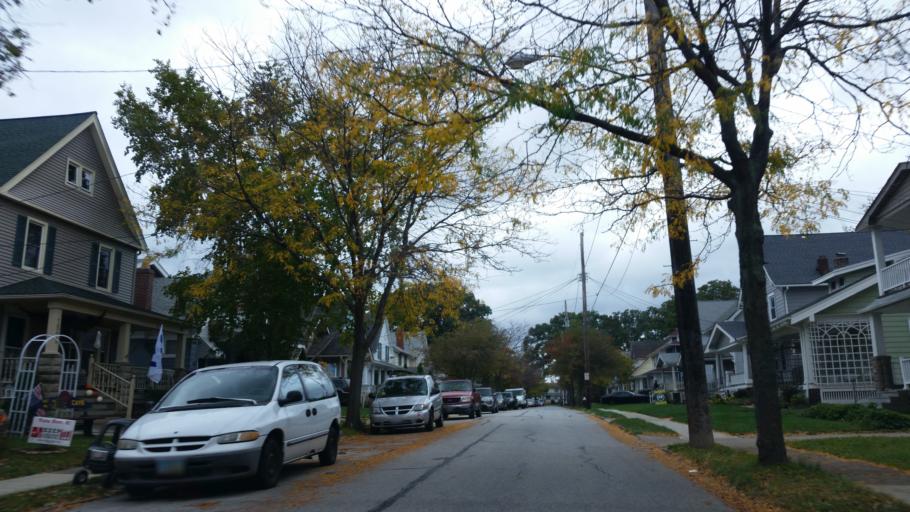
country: US
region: Ohio
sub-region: Cuyahoga County
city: Lakewood
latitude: 41.4825
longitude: -81.8177
